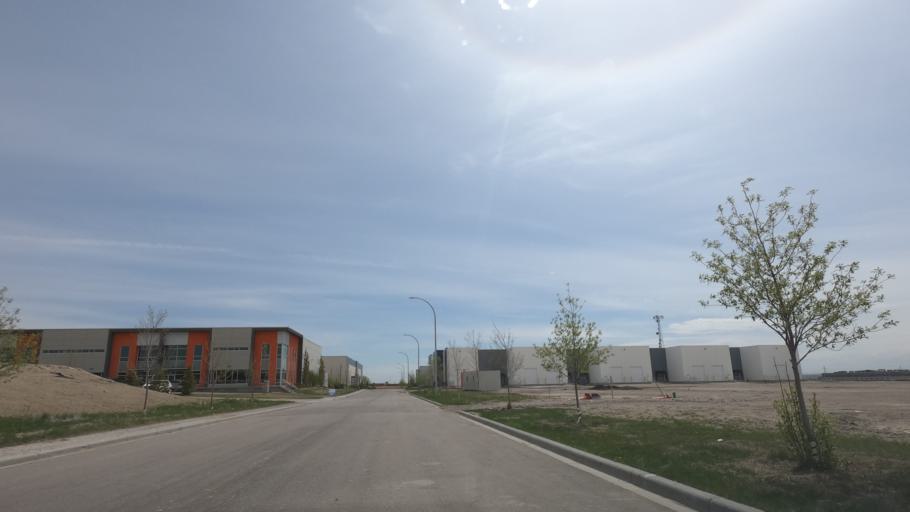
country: CA
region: Alberta
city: Airdrie
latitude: 51.3055
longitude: -113.9848
